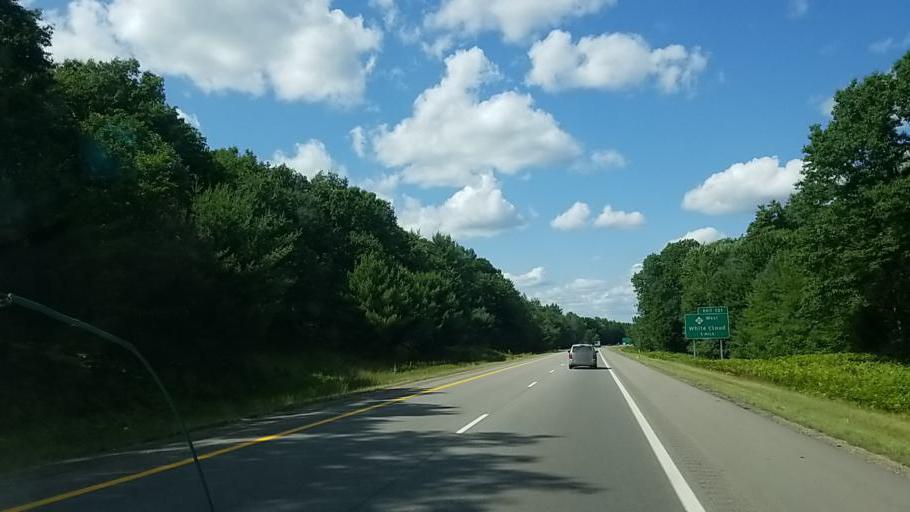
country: US
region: Michigan
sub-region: Mecosta County
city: Big Rapids
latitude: 43.5617
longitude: -85.4896
